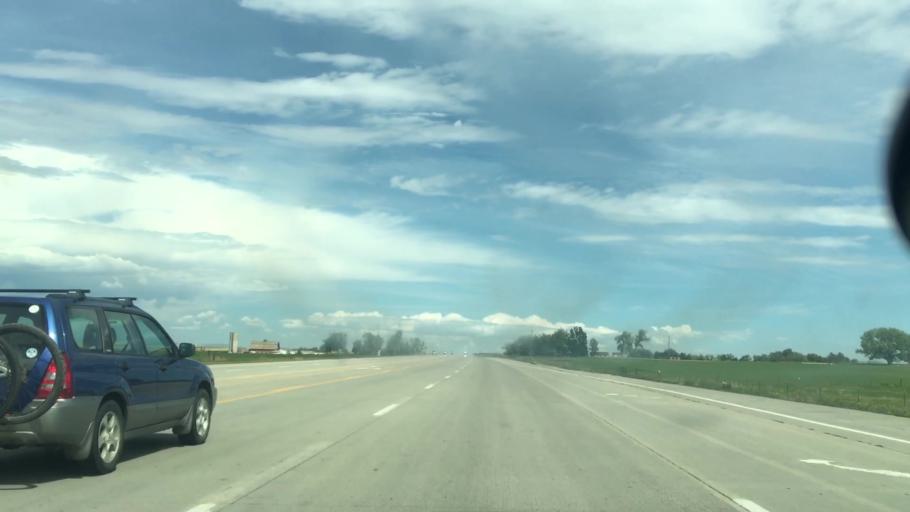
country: US
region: Colorado
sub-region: Boulder County
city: Longmont
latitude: 40.2095
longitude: -105.1023
